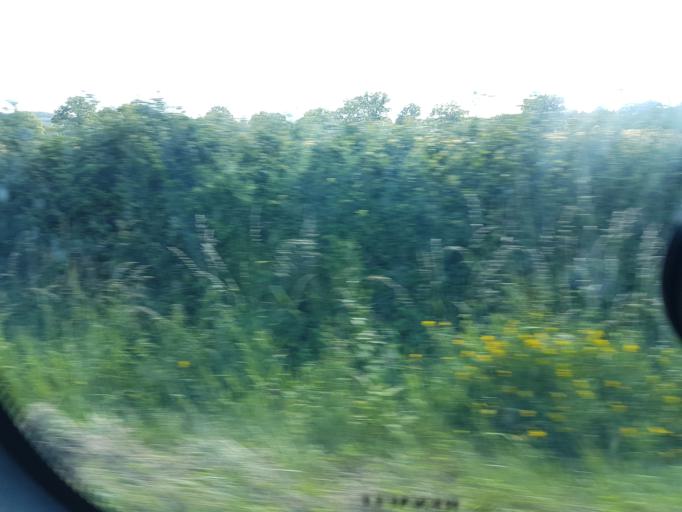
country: FR
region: Bourgogne
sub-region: Departement de Saone-et-Loire
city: Epinac
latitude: 47.0037
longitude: 4.4759
